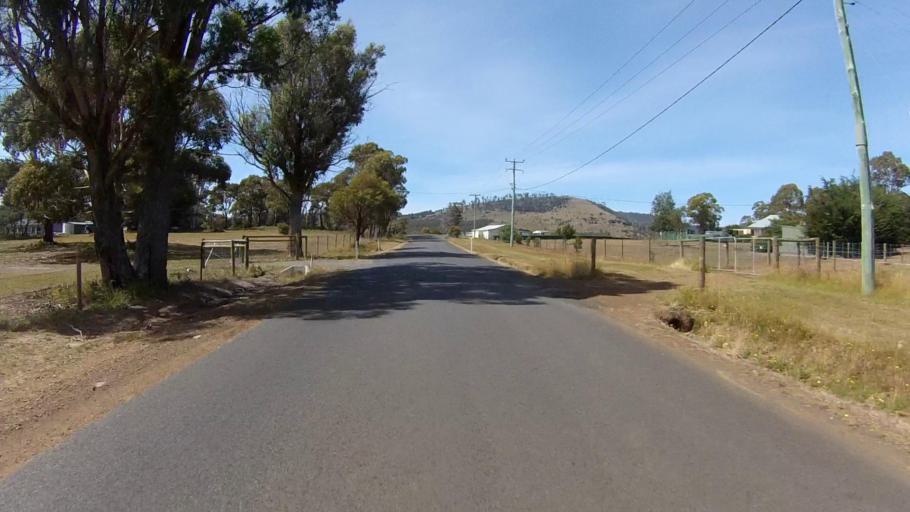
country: AU
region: Tasmania
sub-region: Sorell
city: Sorell
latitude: -42.6142
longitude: 147.7274
